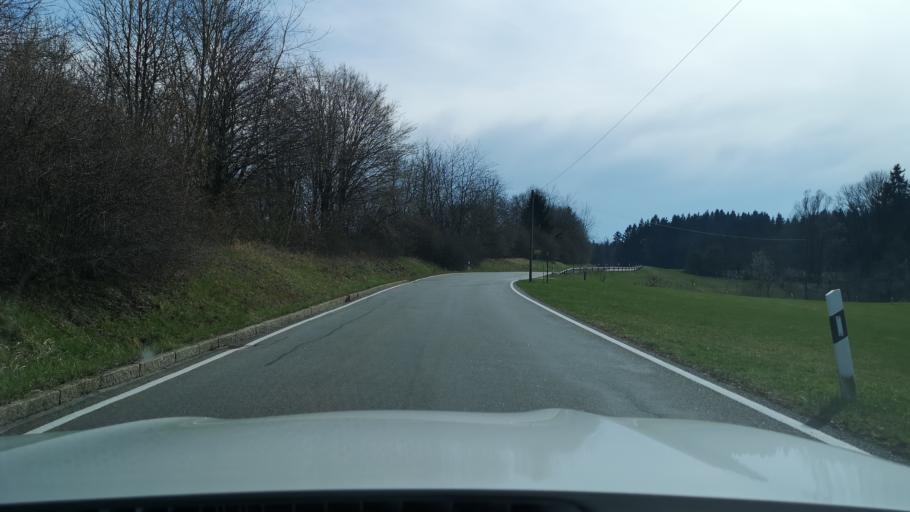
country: DE
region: Bavaria
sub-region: Upper Bavaria
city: Isen
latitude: 48.1836
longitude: 12.0462
